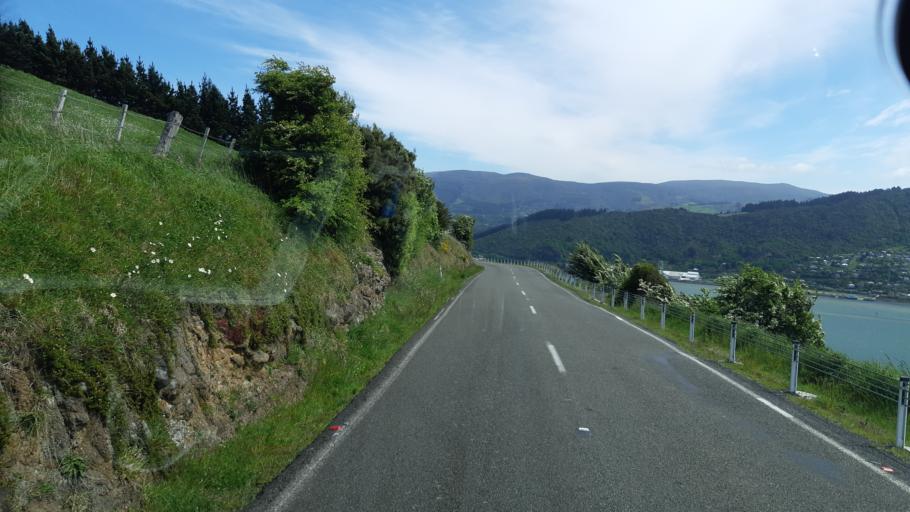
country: NZ
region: Otago
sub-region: Dunedin City
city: Dunedin
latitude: -45.8843
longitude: 170.5601
